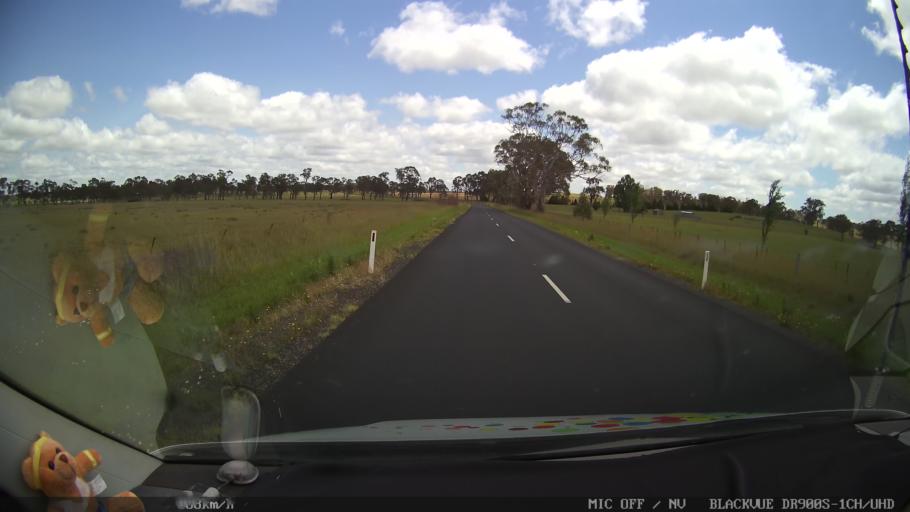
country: AU
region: New South Wales
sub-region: Glen Innes Severn
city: Glen Innes
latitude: -29.6543
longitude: 151.6934
